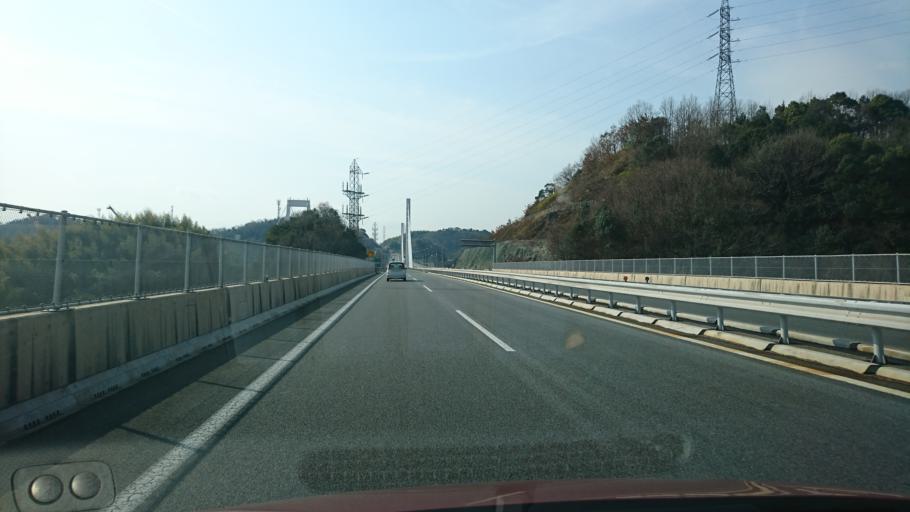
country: JP
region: Hiroshima
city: Onomichi
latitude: 34.4125
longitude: 133.2188
